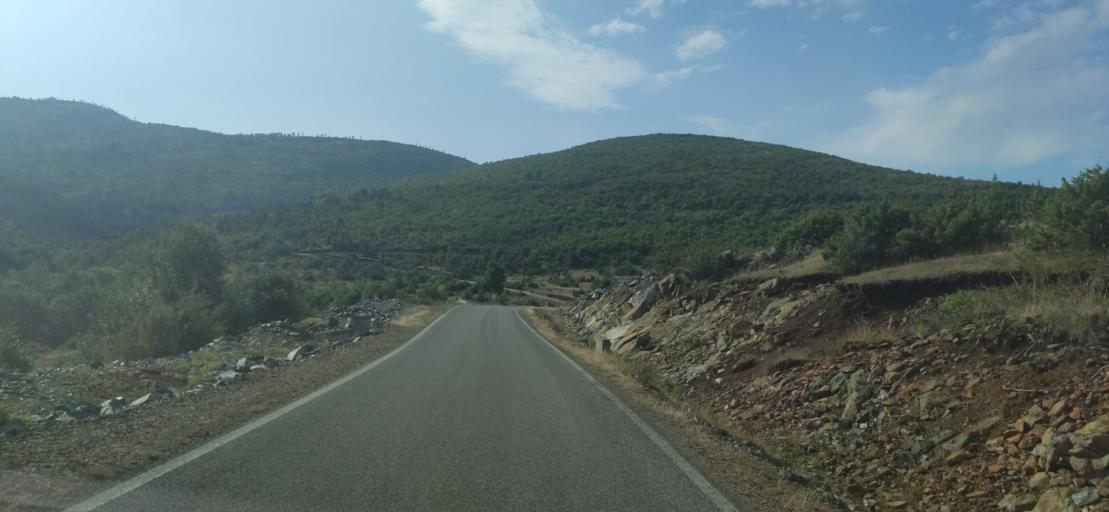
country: AL
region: Shkoder
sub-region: Rrethi i Pukes
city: Iballe
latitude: 42.1797
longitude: 20.0010
